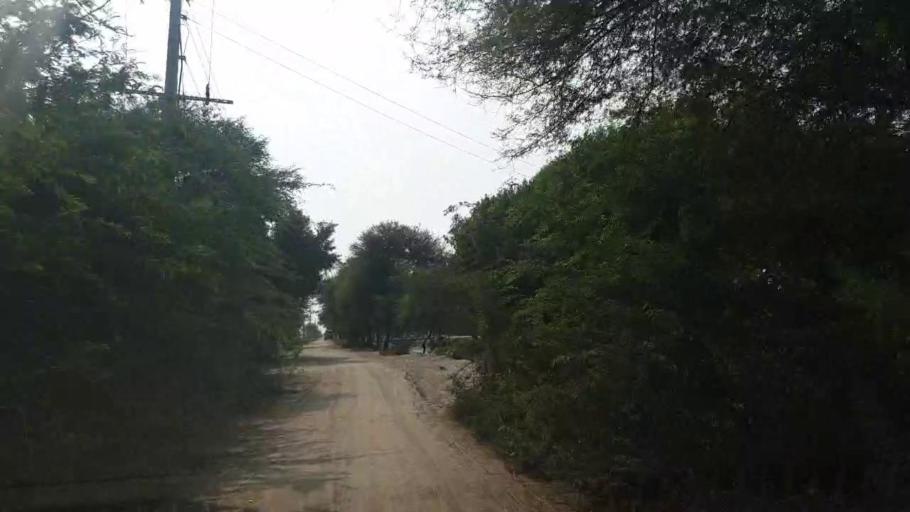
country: PK
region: Sindh
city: Badin
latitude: 24.6179
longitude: 68.7232
